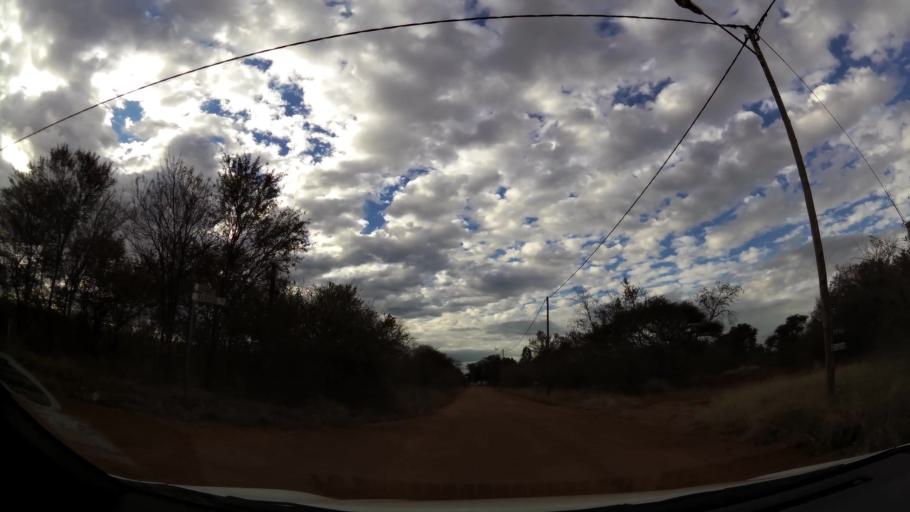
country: ZA
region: Limpopo
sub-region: Waterberg District Municipality
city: Modimolle
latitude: -24.5052
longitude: 28.7227
